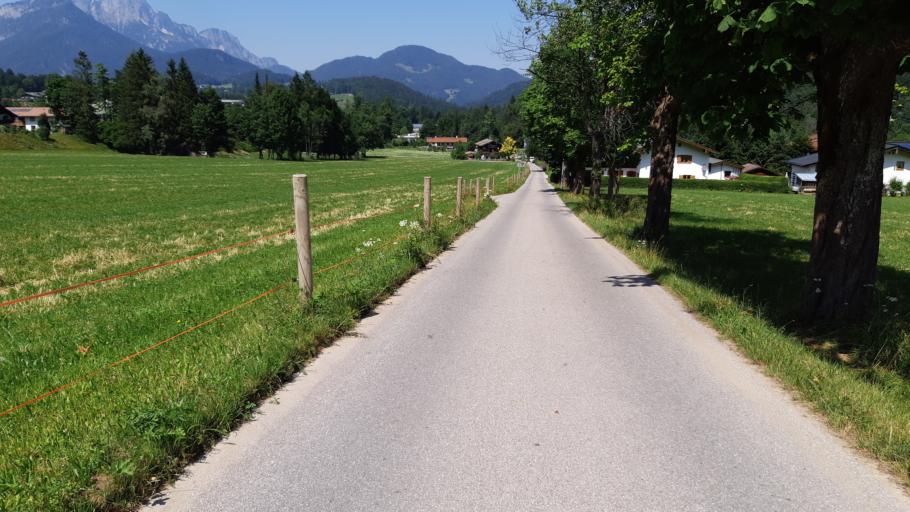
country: DE
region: Bavaria
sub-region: Upper Bavaria
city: Schoenau am Koenigssee
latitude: 47.5956
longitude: 12.9819
